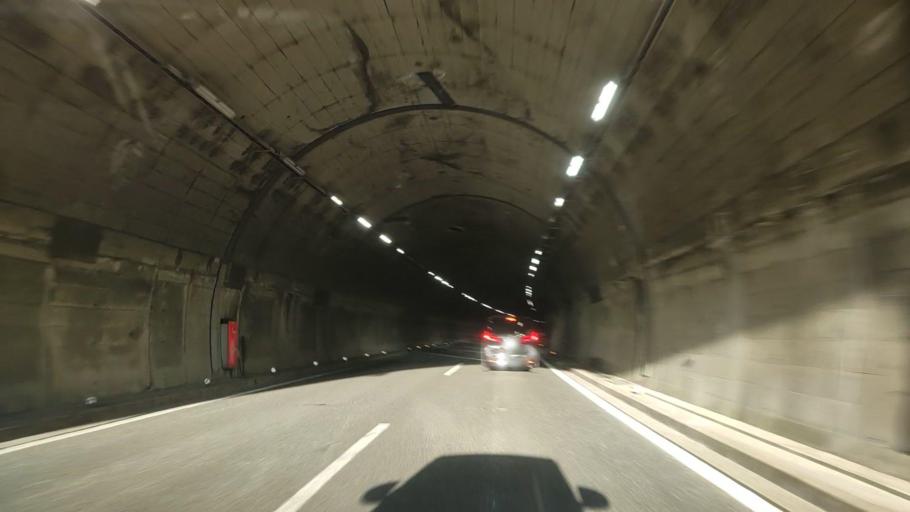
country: JP
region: Hyogo
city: Kariya
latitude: 34.7874
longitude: 134.4002
